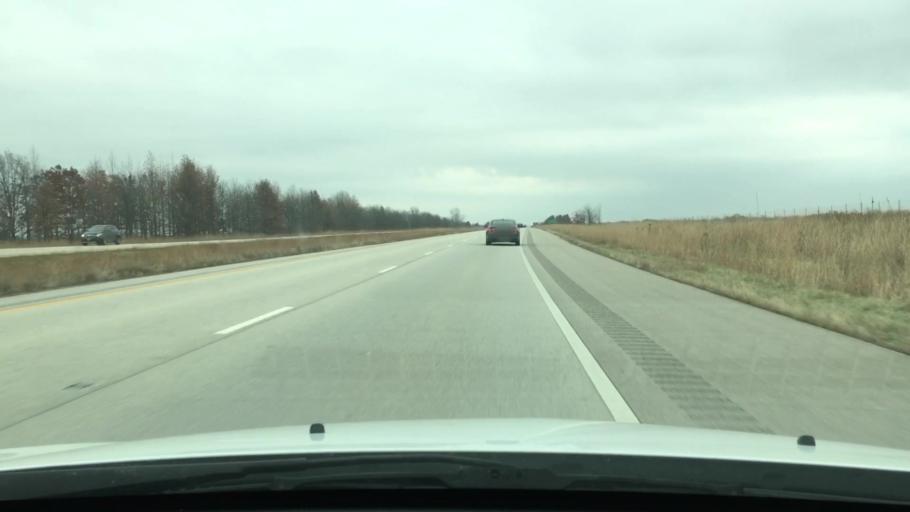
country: US
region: Illinois
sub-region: Sangamon County
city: Jerome
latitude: 39.7515
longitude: -89.7961
